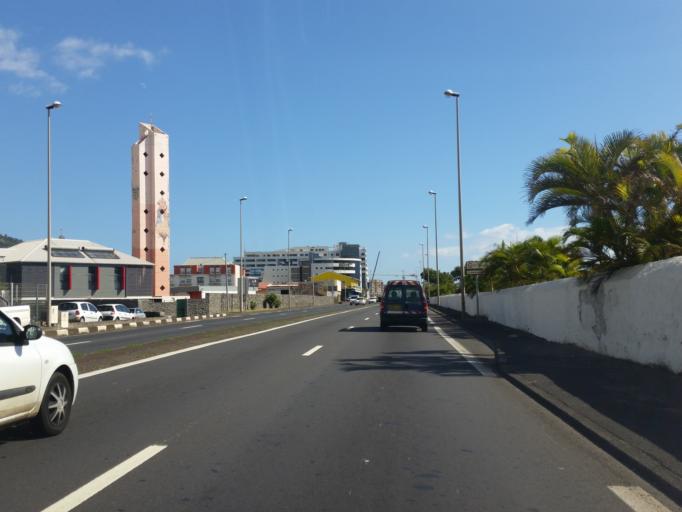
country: RE
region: Reunion
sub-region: Reunion
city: Saint-Denis
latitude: -20.8817
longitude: 55.4629
